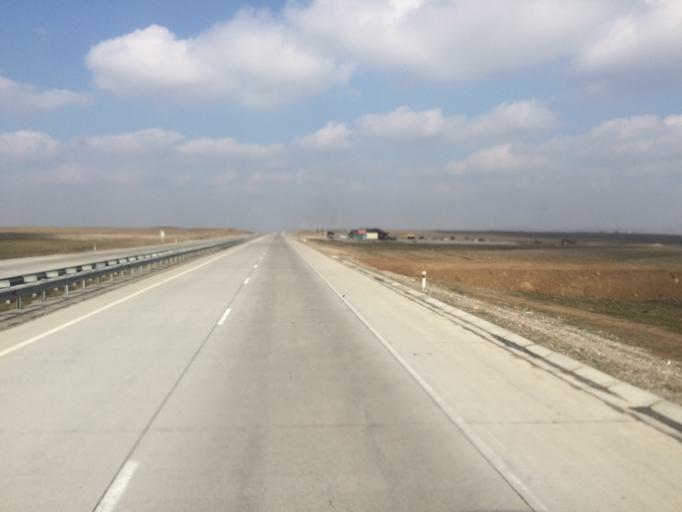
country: KZ
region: Ongtustik Qazaqstan
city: Temirlanovka
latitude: 42.5664
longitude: 69.3109
